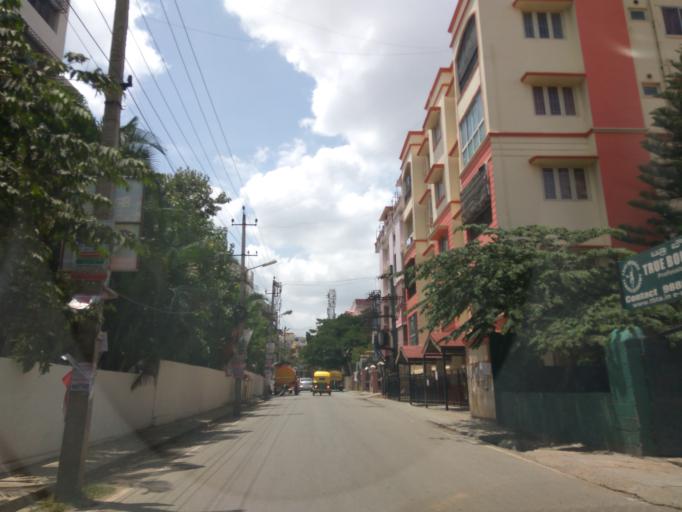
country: IN
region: Karnataka
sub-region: Bangalore Urban
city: Bangalore
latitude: 12.9805
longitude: 77.6759
